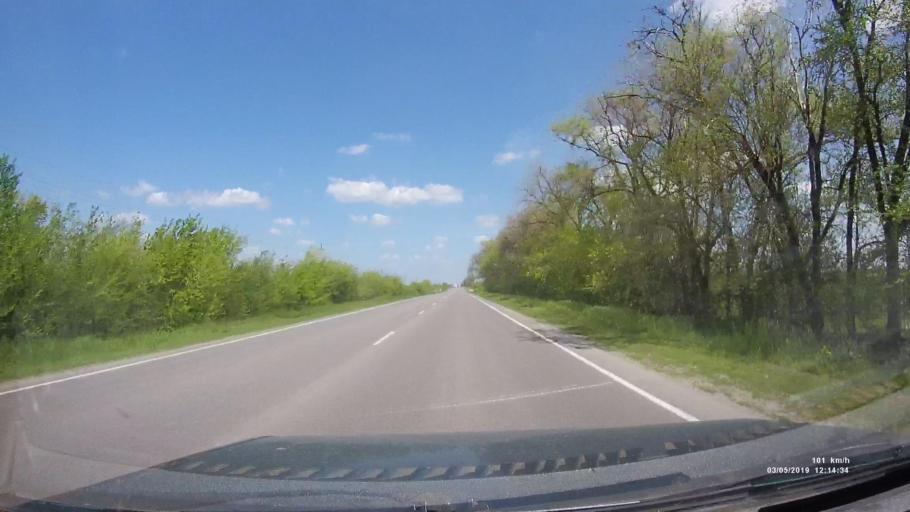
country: RU
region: Rostov
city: Melikhovskaya
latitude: 47.3458
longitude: 40.5647
